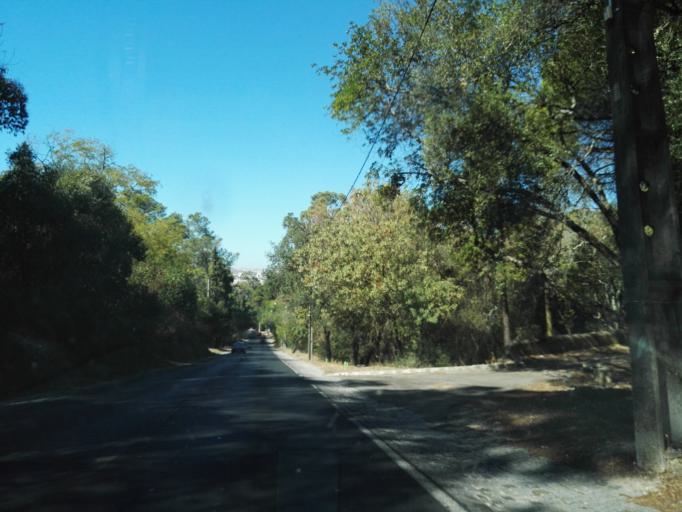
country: PT
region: Lisbon
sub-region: Odivelas
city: Pontinha
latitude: 38.7339
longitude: -9.1986
